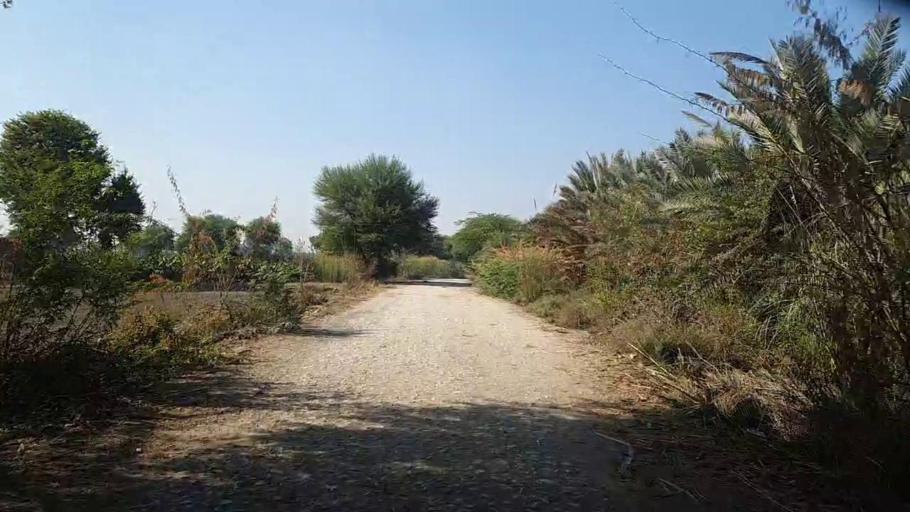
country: PK
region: Sindh
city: Bozdar
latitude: 27.1946
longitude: 68.6668
